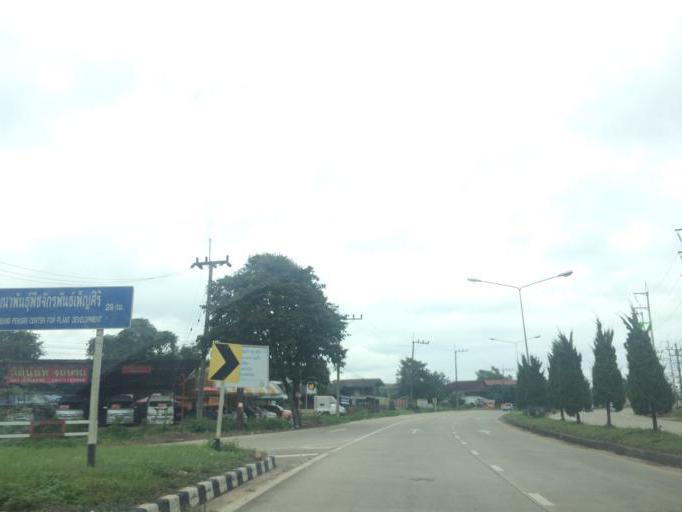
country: TH
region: Chiang Rai
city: Mae Chan
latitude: 20.1382
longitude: 99.8569
